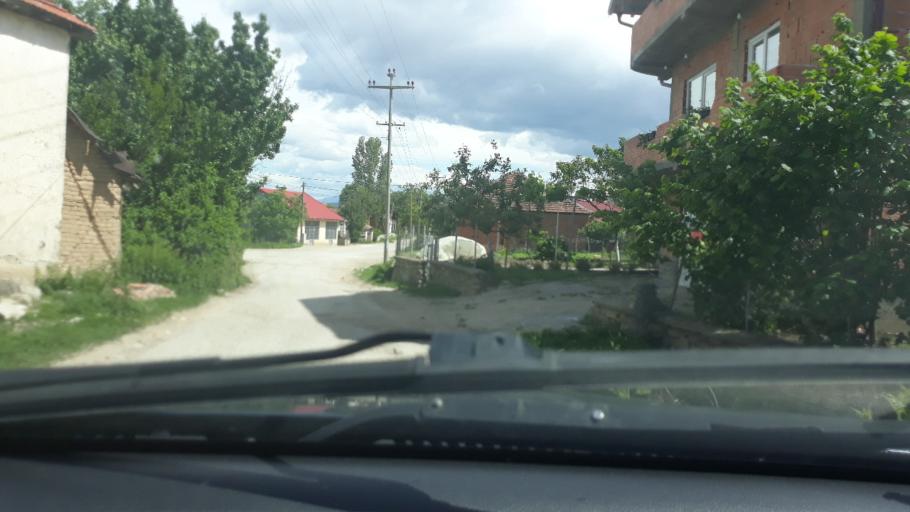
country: MK
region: Krivogastani
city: Krivogashtani
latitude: 41.3213
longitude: 21.3055
